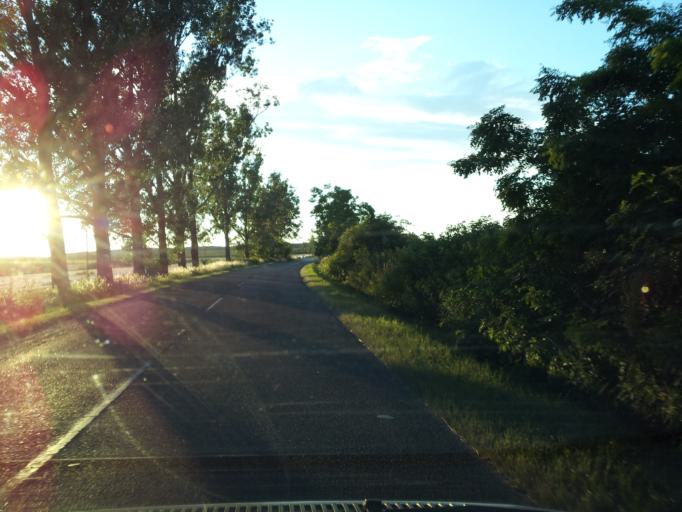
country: HU
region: Veszprem
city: Szentkiralyszabadja
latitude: 47.0303
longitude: 17.9361
